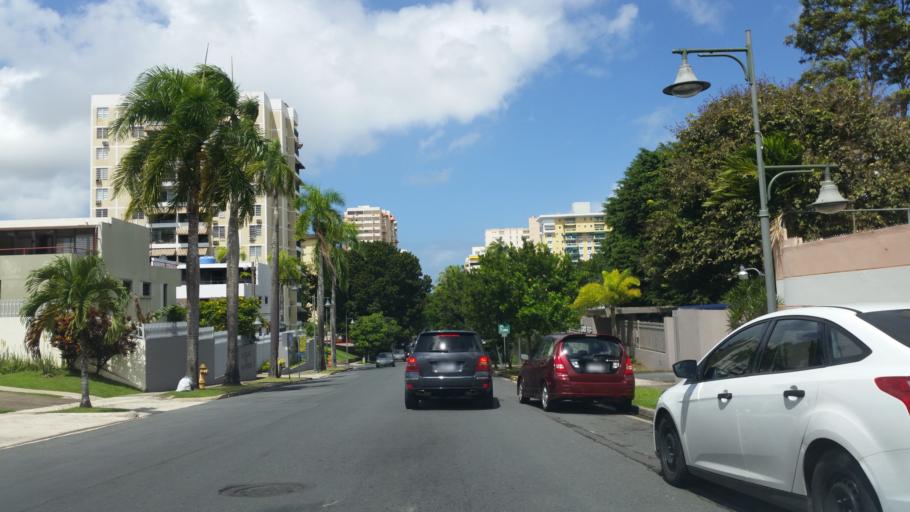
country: PR
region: Catano
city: Catano
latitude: 18.4015
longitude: -66.0988
